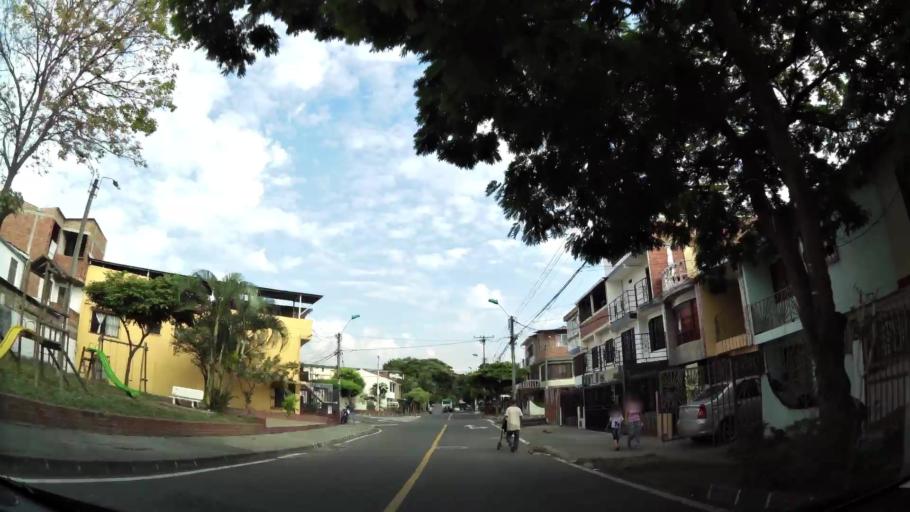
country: CO
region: Valle del Cauca
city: Cali
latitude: 3.4803
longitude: -76.4908
